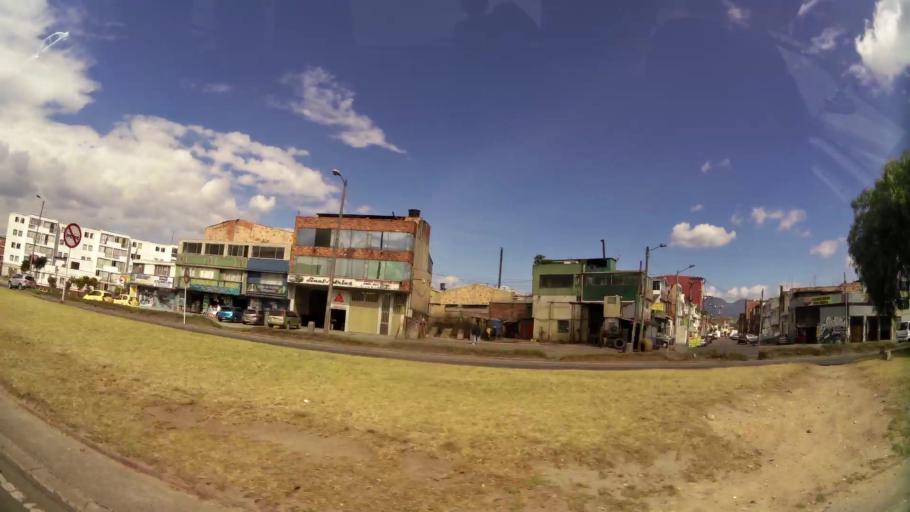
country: CO
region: Bogota D.C.
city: Bogota
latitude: 4.6162
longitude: -74.1402
